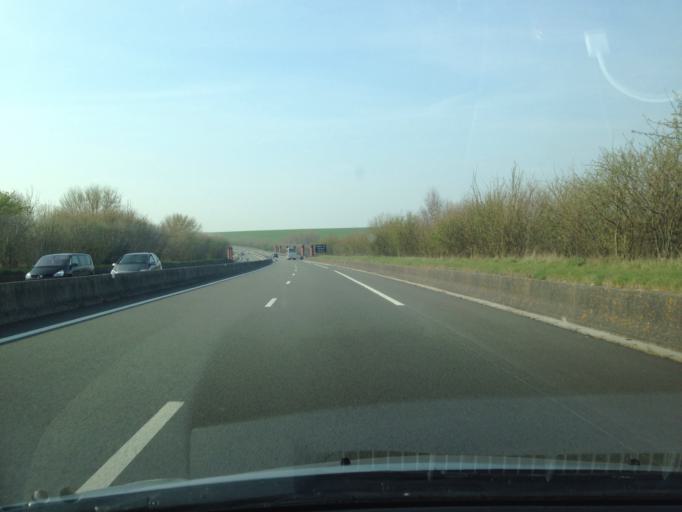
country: FR
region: Picardie
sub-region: Departement de la Somme
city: Rue
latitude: 50.3218
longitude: 1.7193
